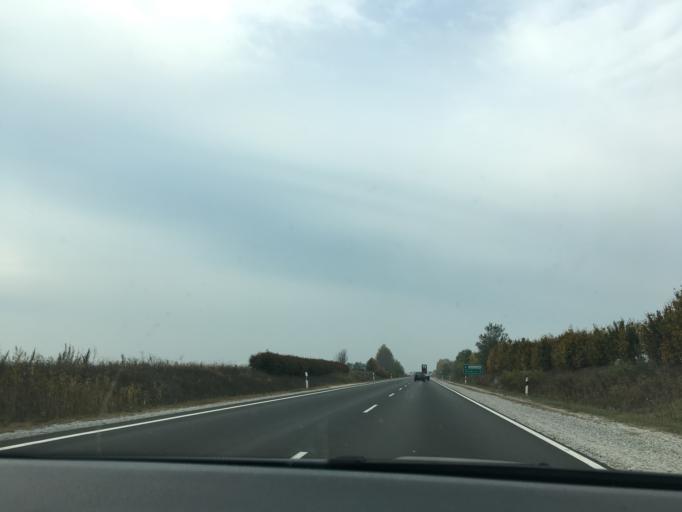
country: HU
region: Pest
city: Abony
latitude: 47.2186
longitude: 20.0259
